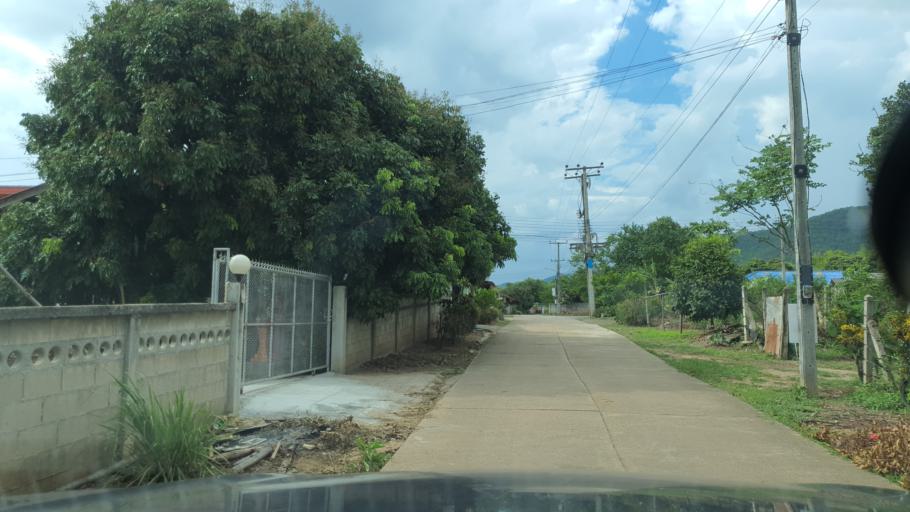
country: TH
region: Chiang Mai
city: Mae Taeng
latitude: 19.1388
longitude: 99.0367
